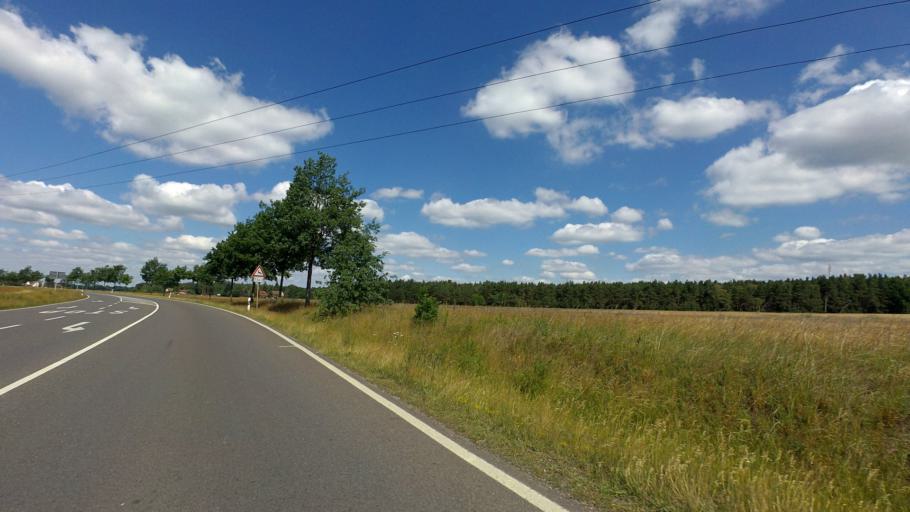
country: DE
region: Brandenburg
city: Grossraschen
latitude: 51.5780
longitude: 14.0830
